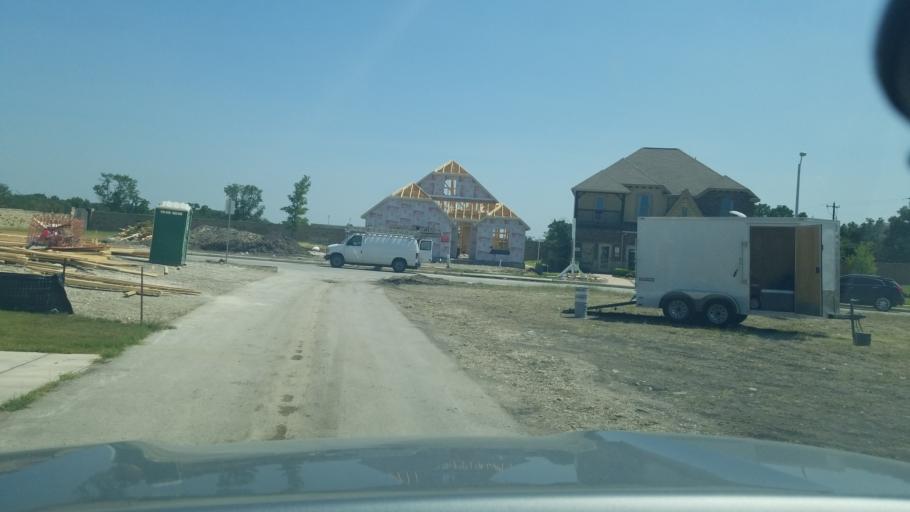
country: US
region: Texas
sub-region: Kendall County
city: Boerne
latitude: 29.7928
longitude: -98.7016
